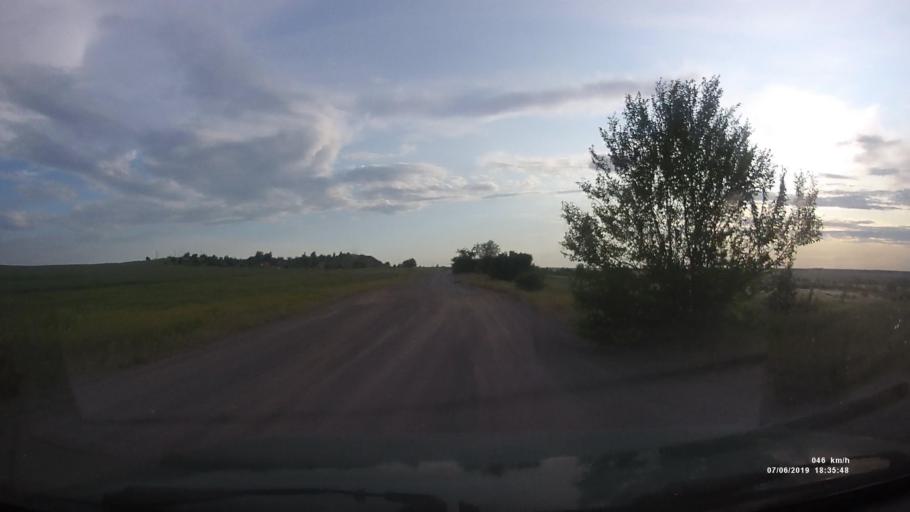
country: RU
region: Rostov
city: Staraya Stanitsa
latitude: 48.2541
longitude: 40.3553
